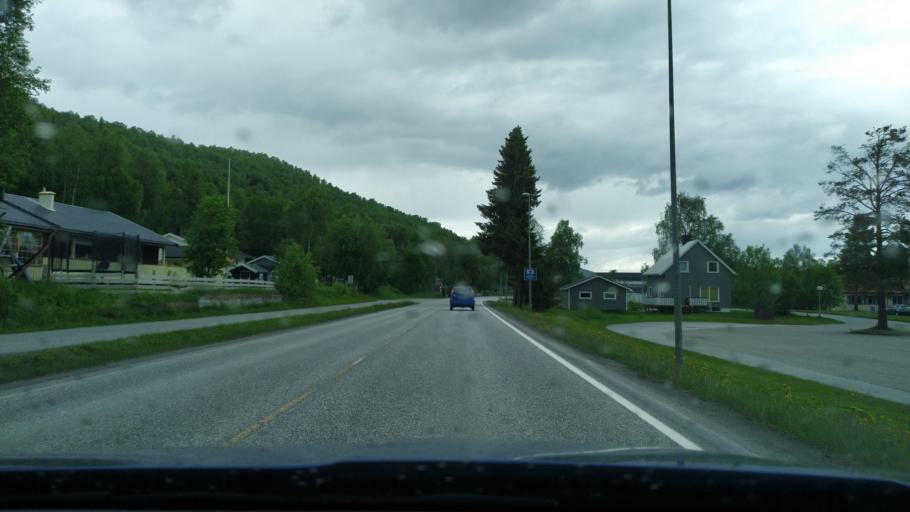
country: NO
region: Troms
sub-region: Malselv
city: Moen
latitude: 69.0299
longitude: 18.5020
